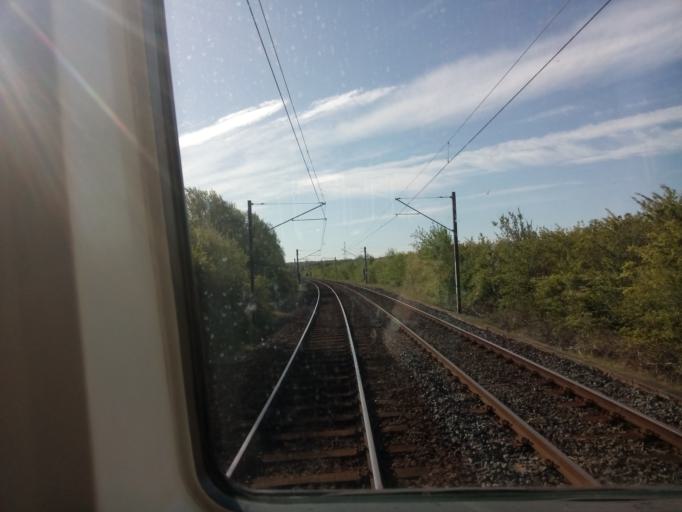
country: GB
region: England
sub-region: Newcastle upon Tyne
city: Dinnington
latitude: 55.0223
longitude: -1.6980
